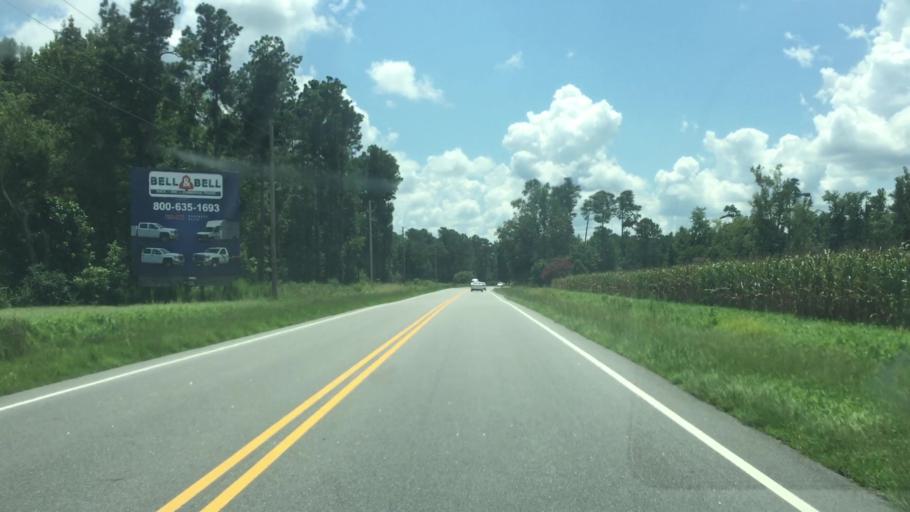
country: US
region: North Carolina
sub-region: Columbus County
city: Tabor City
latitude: 34.2191
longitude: -78.8241
